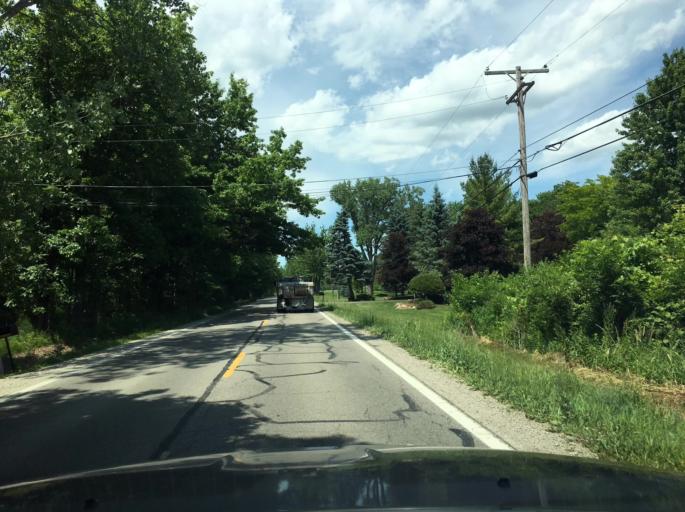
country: US
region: Michigan
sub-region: Macomb County
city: Romeo
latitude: 42.7518
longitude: -82.9608
